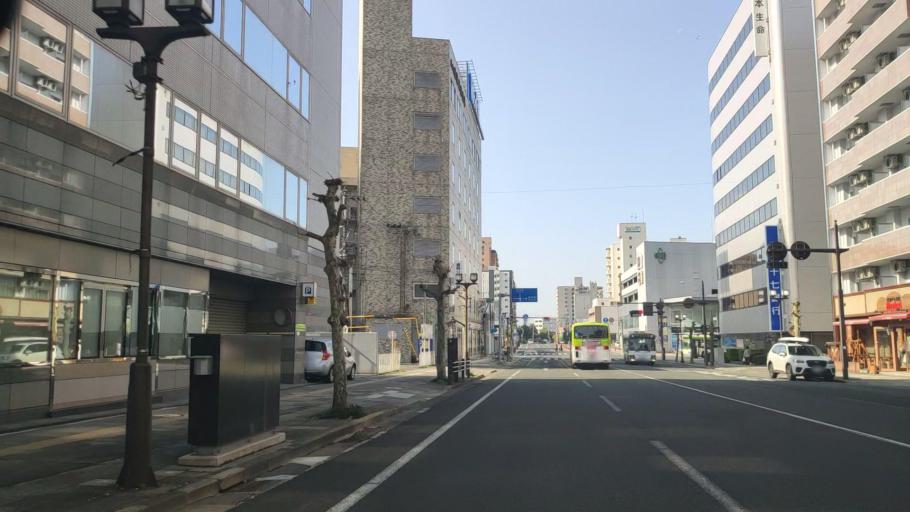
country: JP
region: Iwate
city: Morioka-shi
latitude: 39.7044
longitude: 141.1438
